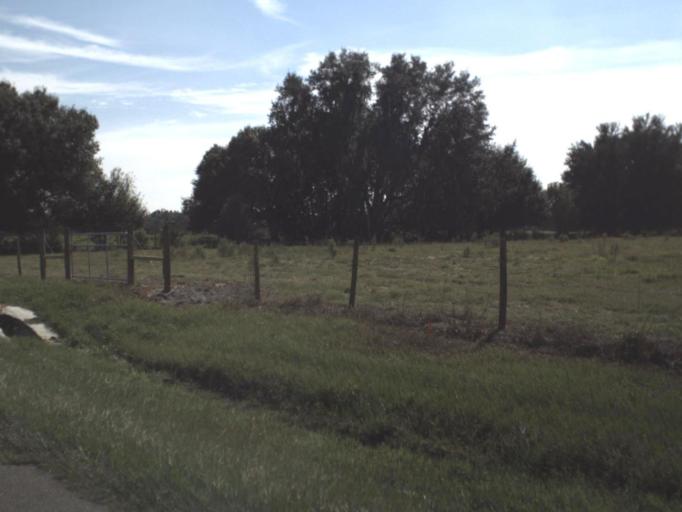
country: US
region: Florida
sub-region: Hardee County
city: Wauchula
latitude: 27.5514
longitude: -81.7559
